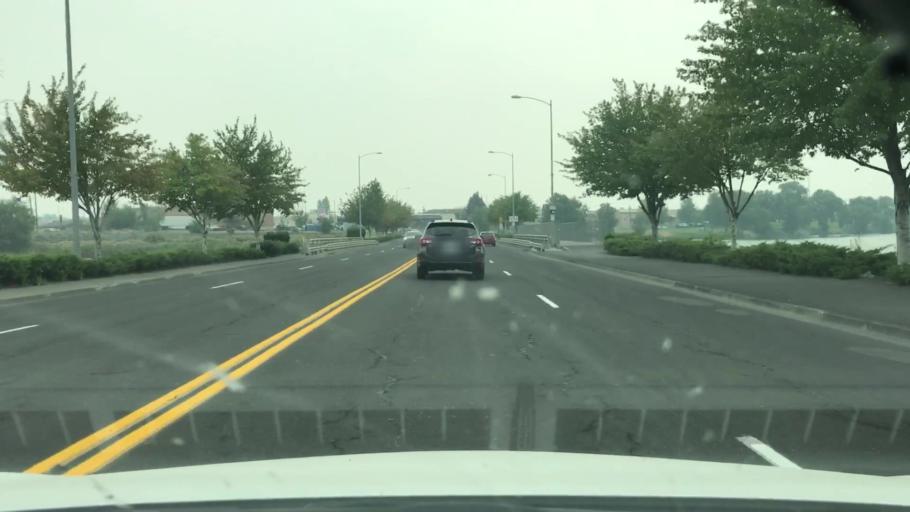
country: US
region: Washington
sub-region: Grant County
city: Moses Lake
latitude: 47.1348
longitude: -119.2785
